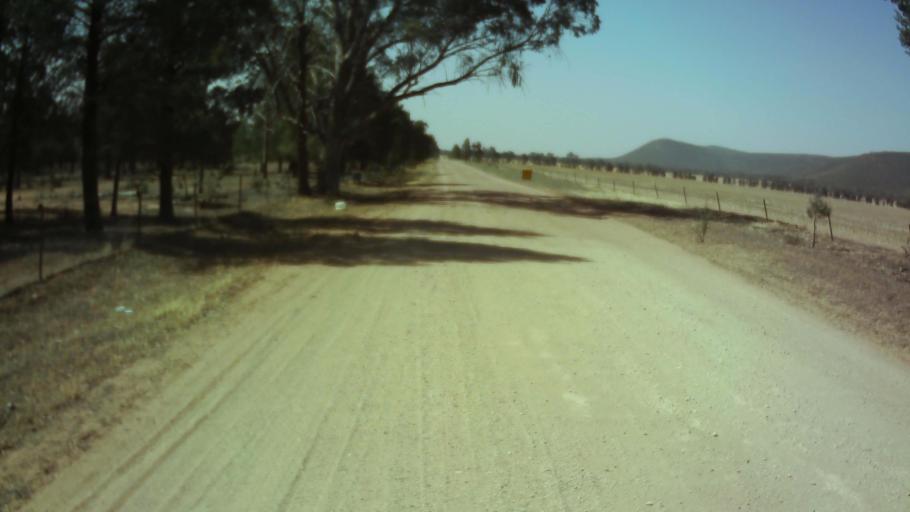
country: AU
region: New South Wales
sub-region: Weddin
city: Grenfell
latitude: -33.9431
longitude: 147.9285
